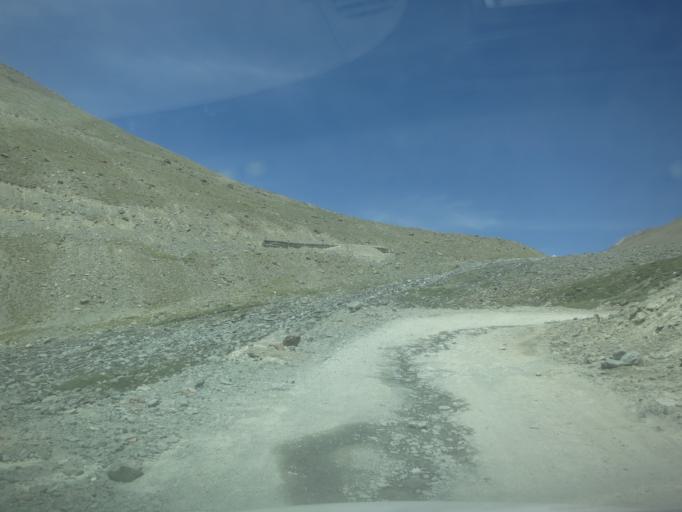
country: IN
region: Himachal Pradesh
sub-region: Kulu
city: Manali
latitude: 32.3885
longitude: 77.6253
